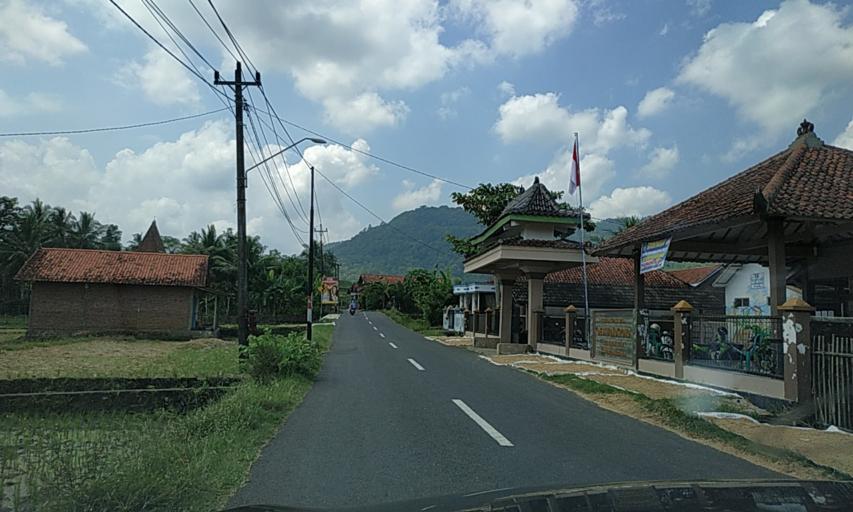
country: ID
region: Central Java
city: Kutoarjo
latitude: -7.6253
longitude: 109.7261
